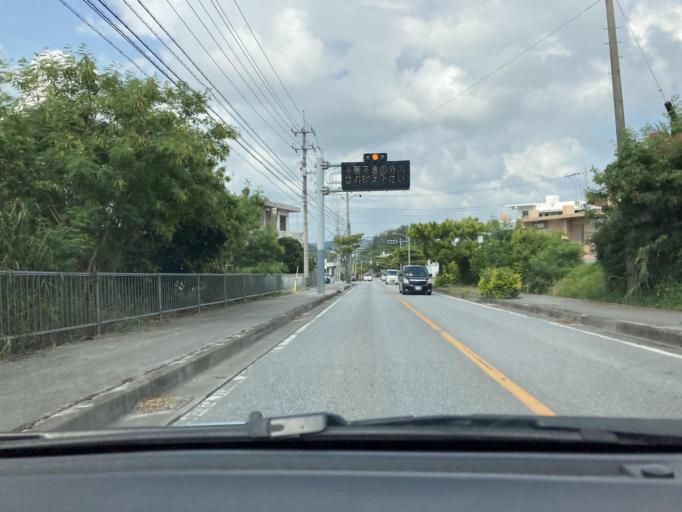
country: JP
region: Okinawa
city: Ginowan
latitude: 26.2672
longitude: 127.7764
